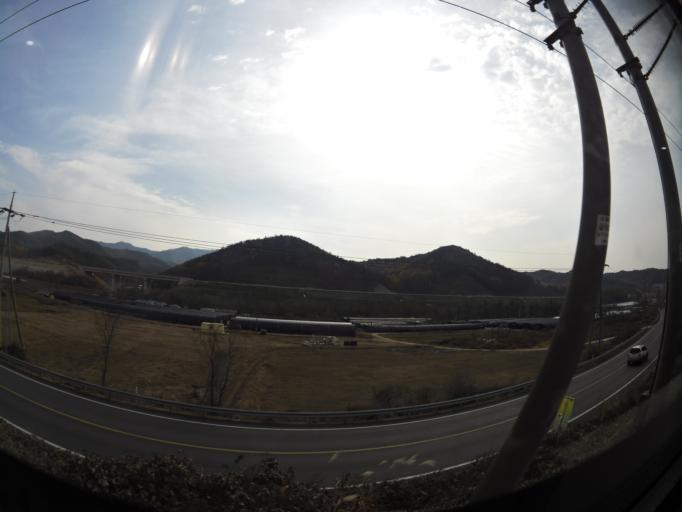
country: KR
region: Chungcheongbuk-do
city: Yong-dong
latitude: 36.1834
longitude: 127.8449
